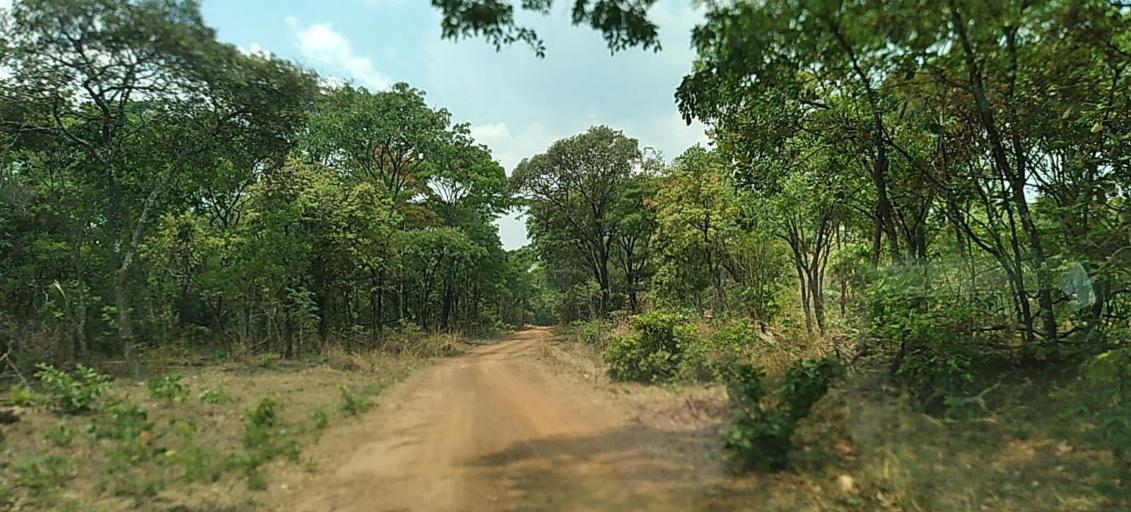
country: ZM
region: Copperbelt
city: Chingola
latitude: -12.7718
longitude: 27.6831
